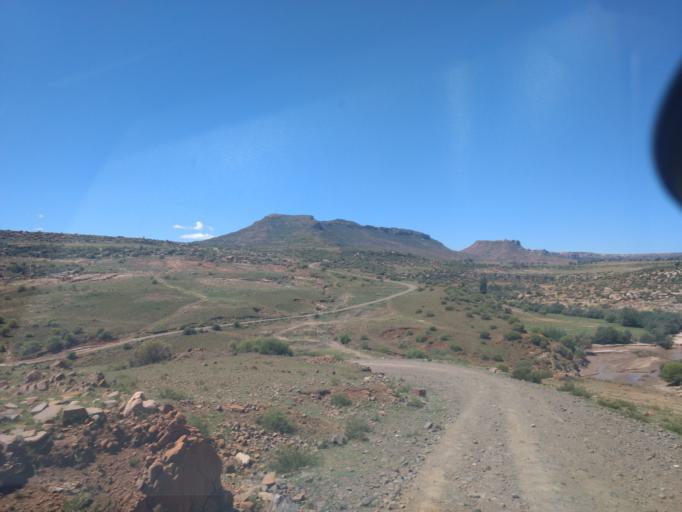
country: LS
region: Maseru
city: Maseru
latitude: -29.4845
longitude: 27.3704
